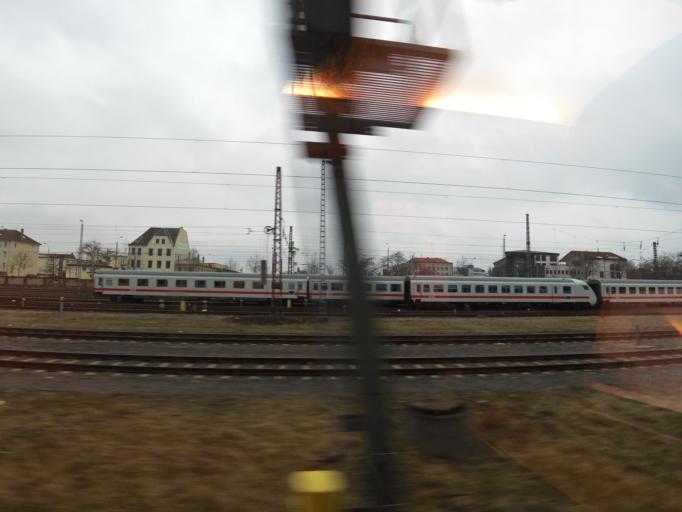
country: DE
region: Saxony
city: Leipzig
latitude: 51.3581
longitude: 12.3964
